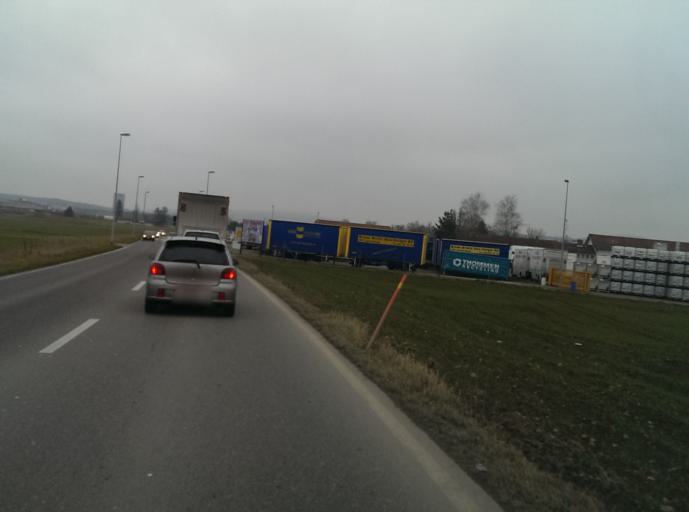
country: CH
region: Zurich
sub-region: Bezirk Dietikon
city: Dietikon / Almend
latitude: 47.4166
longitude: 8.3802
